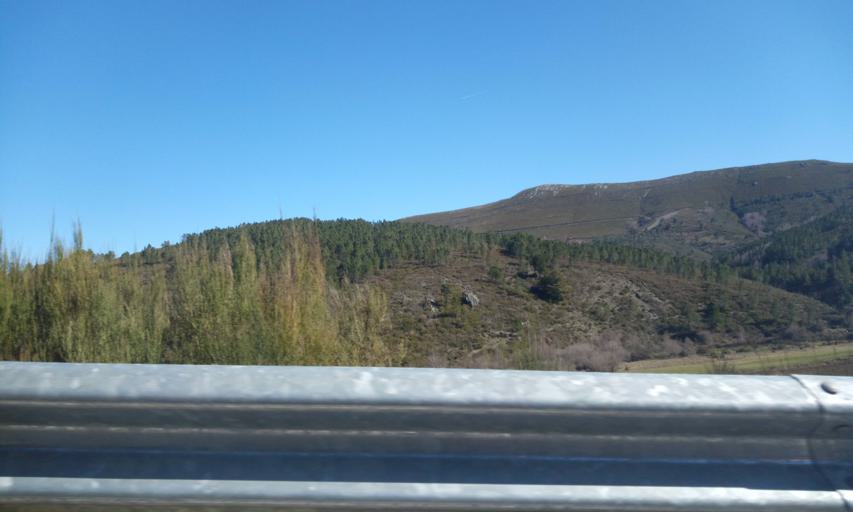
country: PT
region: Guarda
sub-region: Manteigas
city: Manteigas
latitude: 40.4469
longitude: -7.5132
